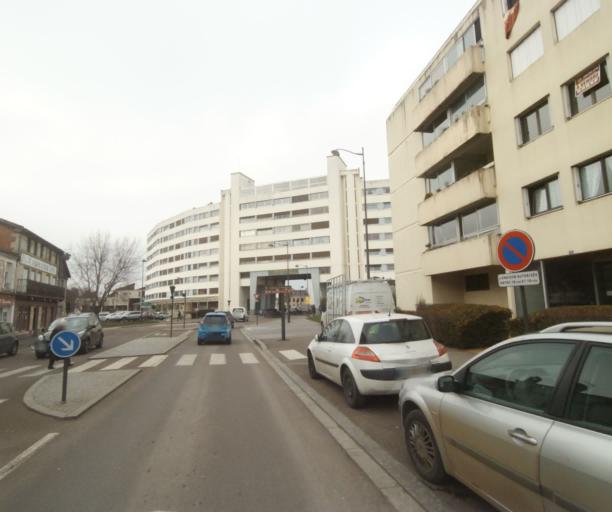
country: FR
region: Champagne-Ardenne
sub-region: Departement de la Haute-Marne
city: Saint-Dizier
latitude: 48.6361
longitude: 4.9576
